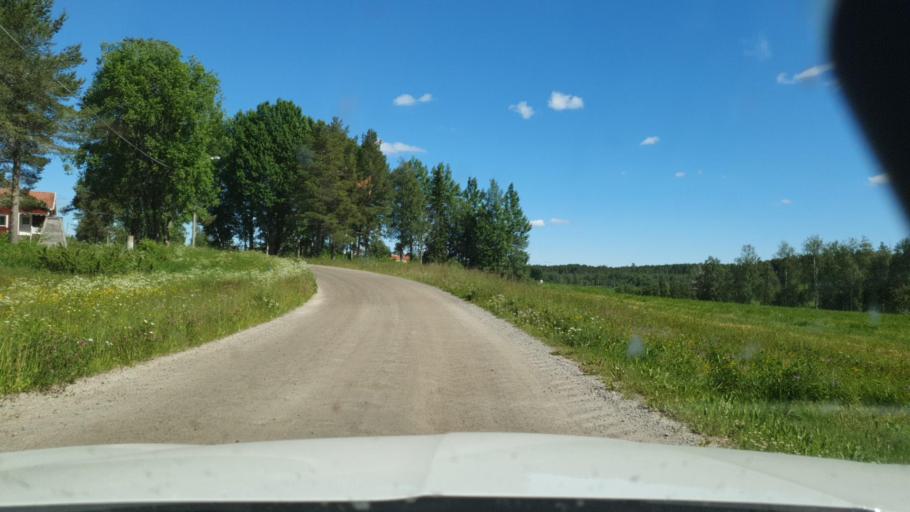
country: SE
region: Vaesterbotten
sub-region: Skelleftea Kommun
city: Byske
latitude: 65.1146
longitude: 21.2023
